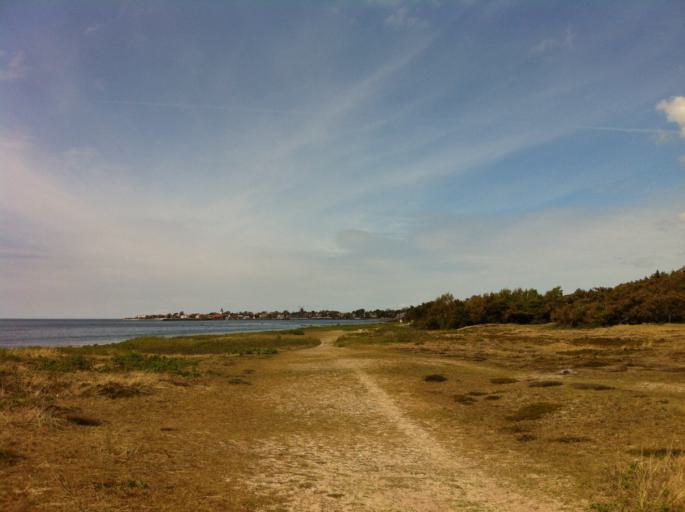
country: DK
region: Capital Region
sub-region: Helsingor Kommune
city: Hellebaek
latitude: 56.1314
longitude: 12.5911
